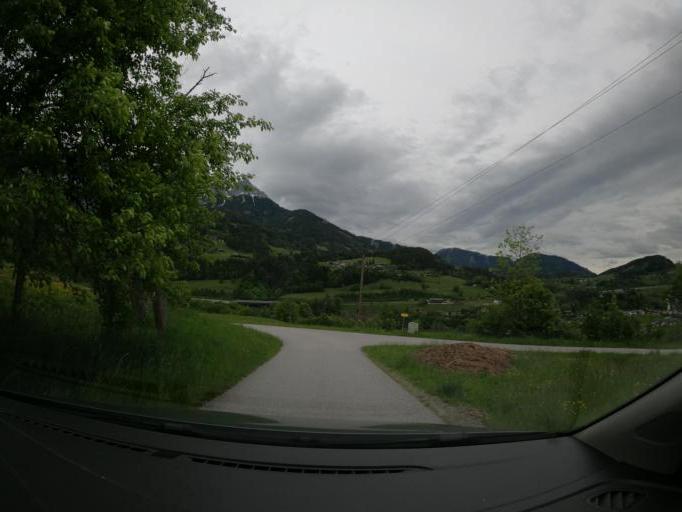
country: AT
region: Salzburg
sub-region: Politischer Bezirk Sankt Johann im Pongau
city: Werfen
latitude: 47.4644
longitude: 13.1940
